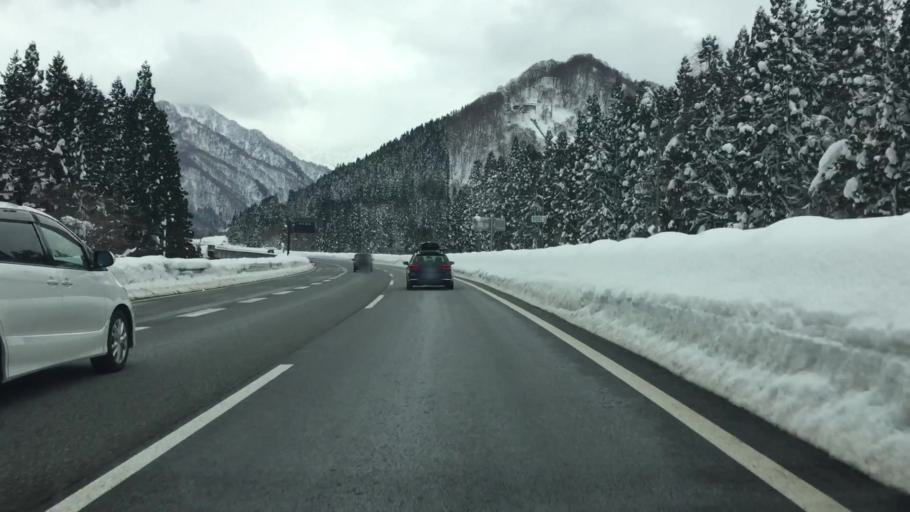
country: JP
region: Niigata
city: Shiozawa
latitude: 36.8824
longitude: 138.8530
